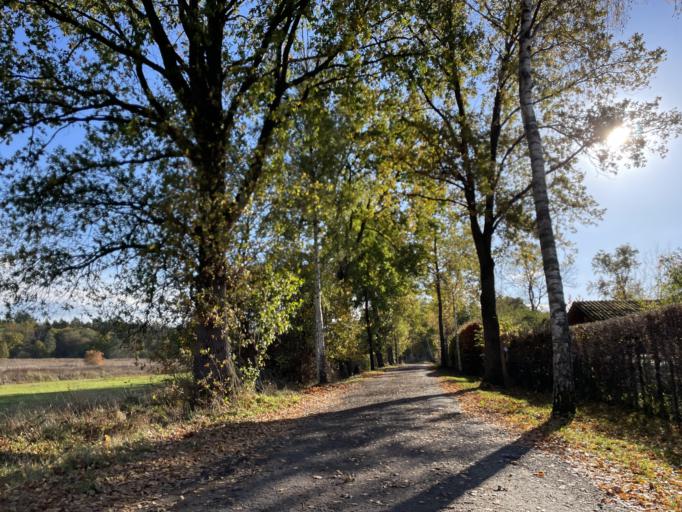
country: DE
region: Lower Saxony
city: Deutsch Evern
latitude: 53.2217
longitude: 10.4187
